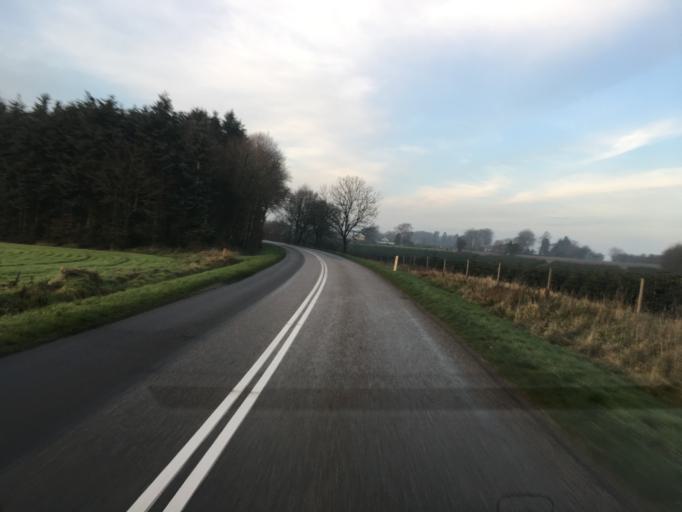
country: DK
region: South Denmark
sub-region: Tonder Kommune
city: Toftlund
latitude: 55.1351
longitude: 9.0621
